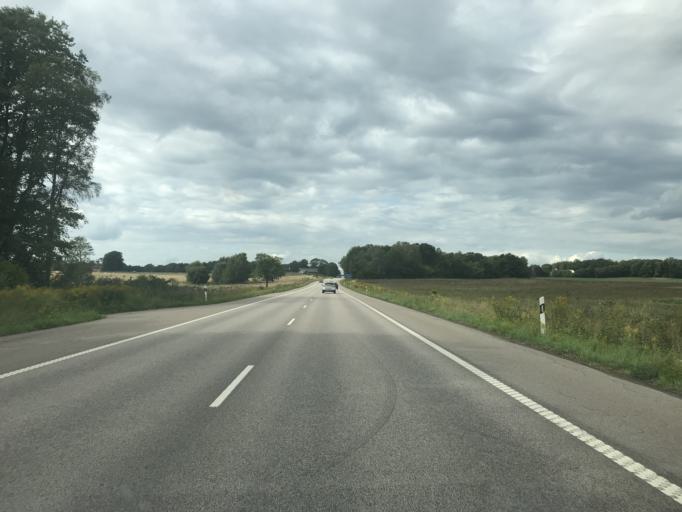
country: SE
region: Skane
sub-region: Hassleholms Kommun
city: Hassleholm
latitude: 56.1353
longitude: 13.8125
